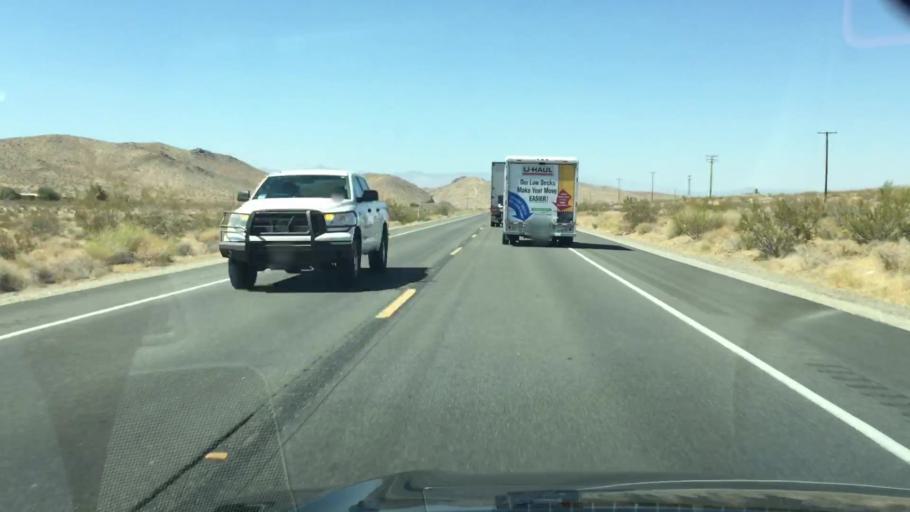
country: US
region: California
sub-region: Kern County
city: Ridgecrest
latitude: 35.5301
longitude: -117.6799
